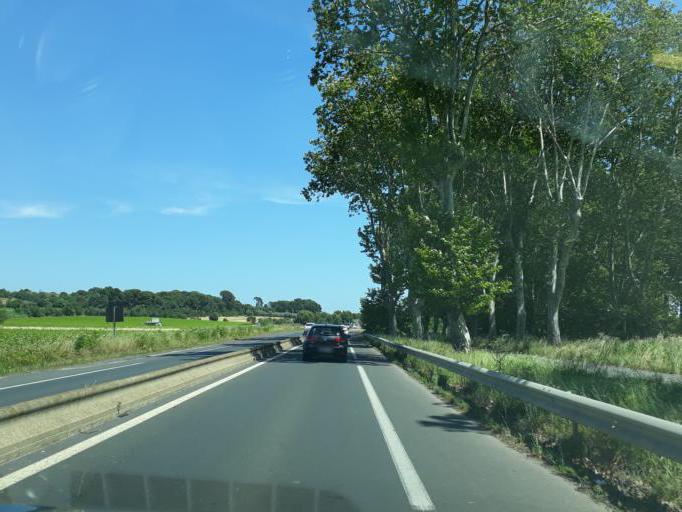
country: FR
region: Languedoc-Roussillon
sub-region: Departement de l'Herault
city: Cers
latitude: 43.3166
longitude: 3.3085
